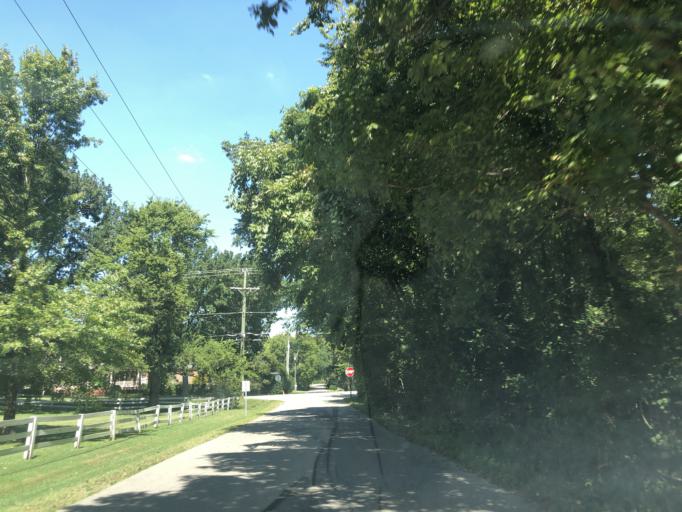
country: US
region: Tennessee
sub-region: Davidson County
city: Oak Hill
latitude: 36.0800
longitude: -86.7991
